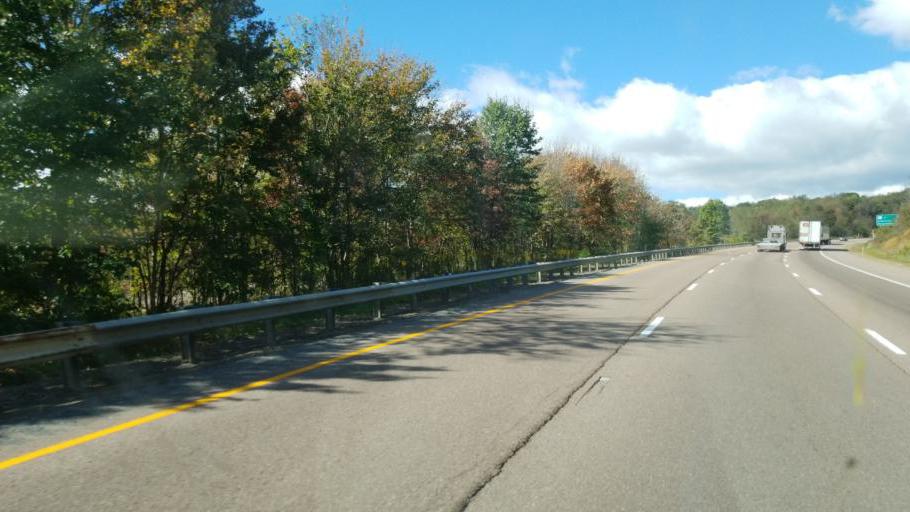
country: US
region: Maryland
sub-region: Allegany County
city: Frostburg
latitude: 39.6449
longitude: -78.9537
